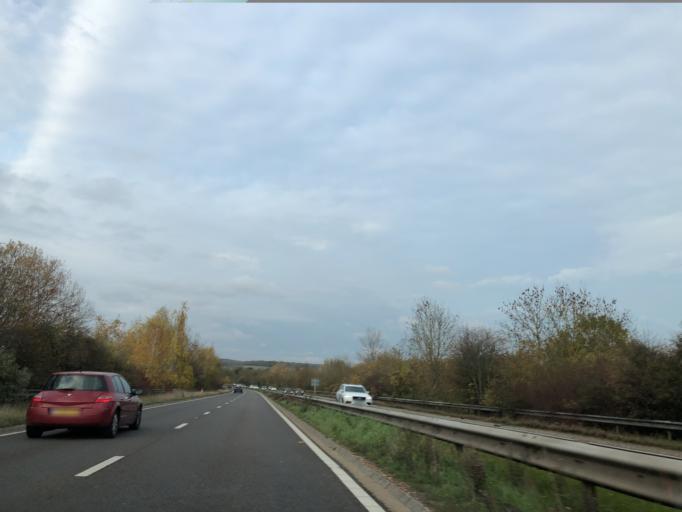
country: GB
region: England
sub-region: Buckinghamshire
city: Marlow
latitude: 51.5715
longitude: -0.7584
